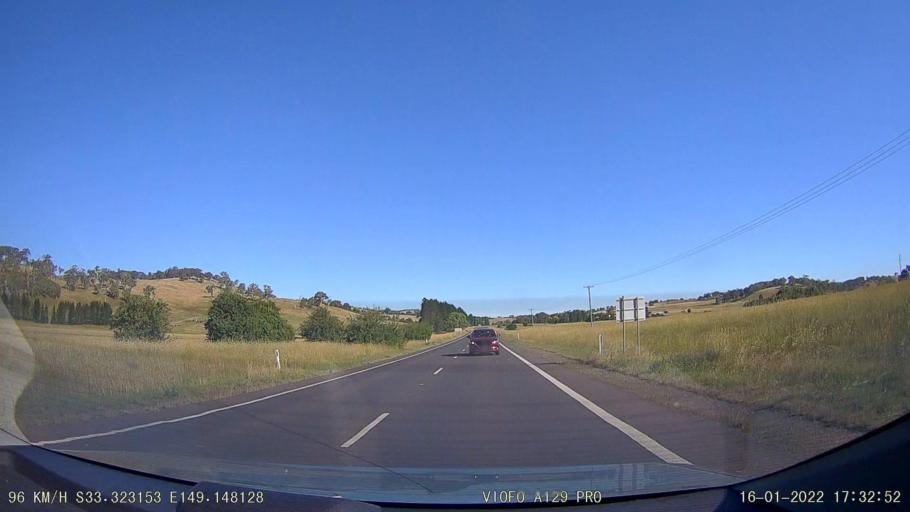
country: AU
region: New South Wales
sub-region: Orange Municipality
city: Orange
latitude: -33.3233
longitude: 149.1481
